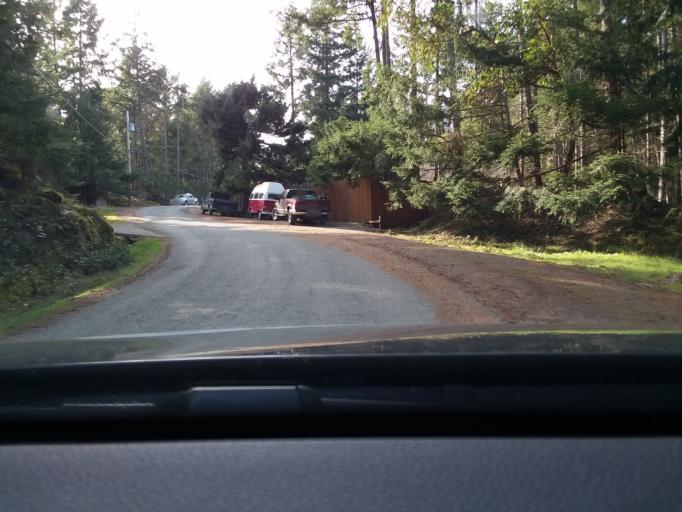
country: CA
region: British Columbia
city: North Saanich
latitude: 48.7694
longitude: -123.2937
